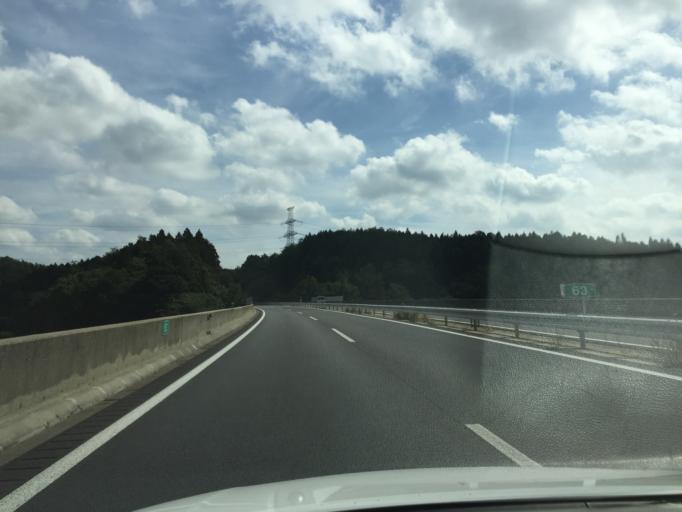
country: JP
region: Fukushima
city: Miharu
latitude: 37.4391
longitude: 140.4461
